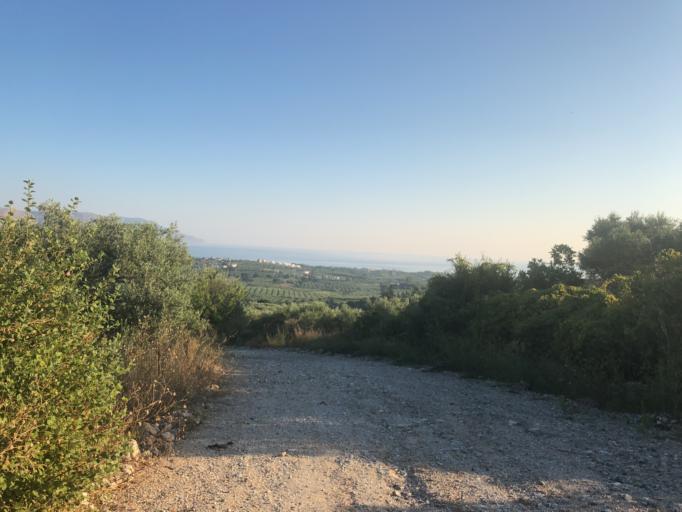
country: GR
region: Crete
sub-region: Nomos Chanias
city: Georgioupolis
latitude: 35.3347
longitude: 24.2913
